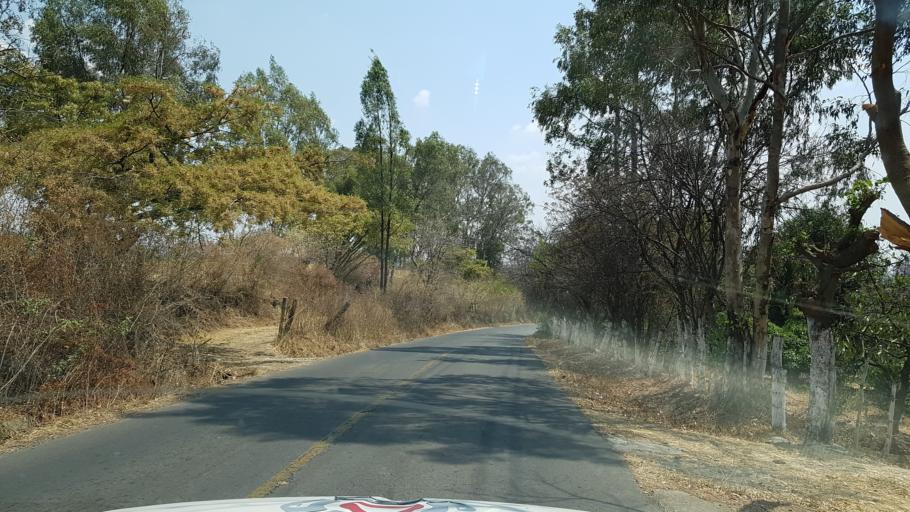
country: MX
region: Morelos
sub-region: Yecapixtla
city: Texcala
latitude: 18.9021
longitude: -98.8095
